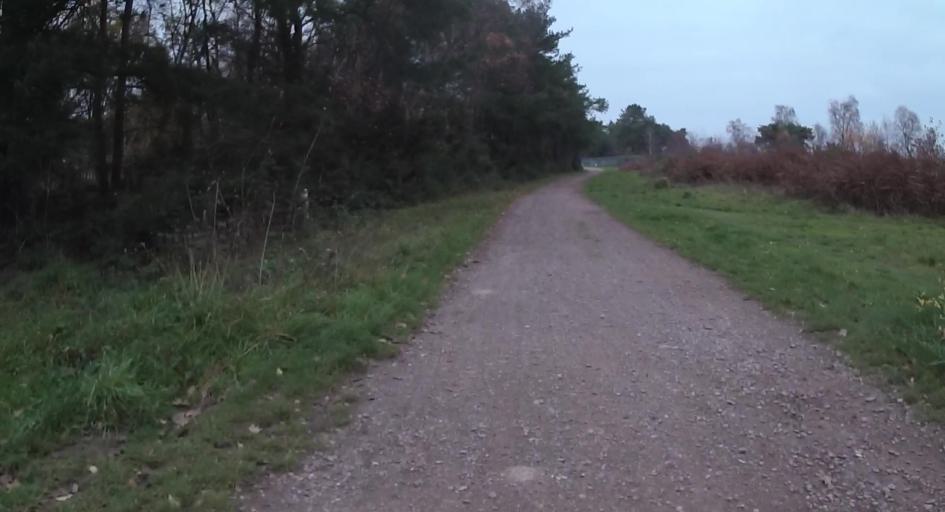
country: GB
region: England
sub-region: Surrey
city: Bagshot
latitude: 51.3252
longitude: -0.6953
